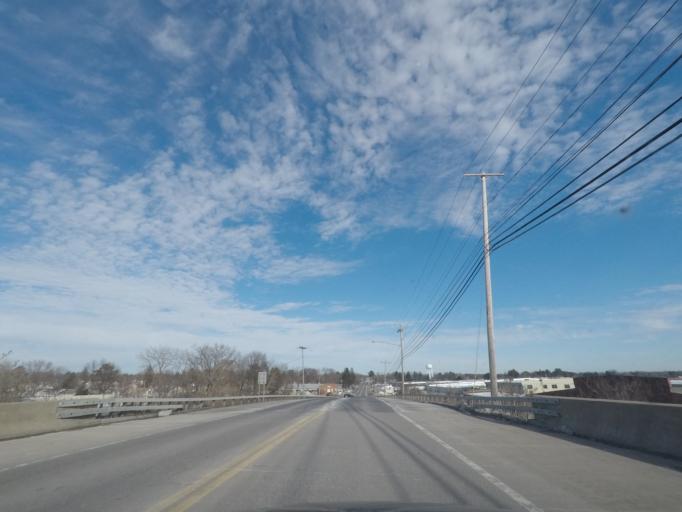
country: US
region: New York
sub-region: Schenectady County
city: Rotterdam
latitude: 42.7874
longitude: -73.9936
